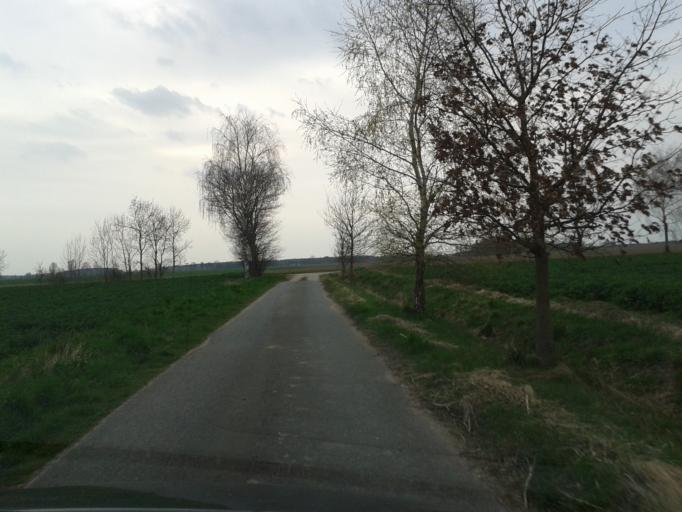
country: DE
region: Lower Saxony
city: Woltersdorf
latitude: 52.9211
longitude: 11.2562
